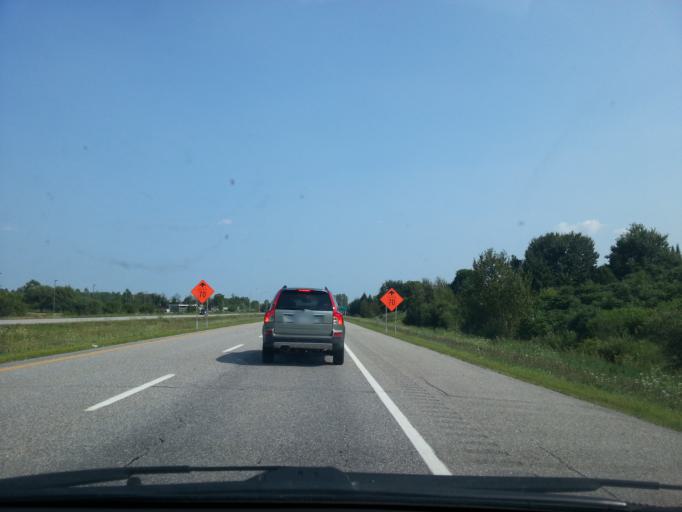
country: CA
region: Quebec
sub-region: Outaouais
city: Gatineau
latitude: 45.4788
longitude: -75.7865
